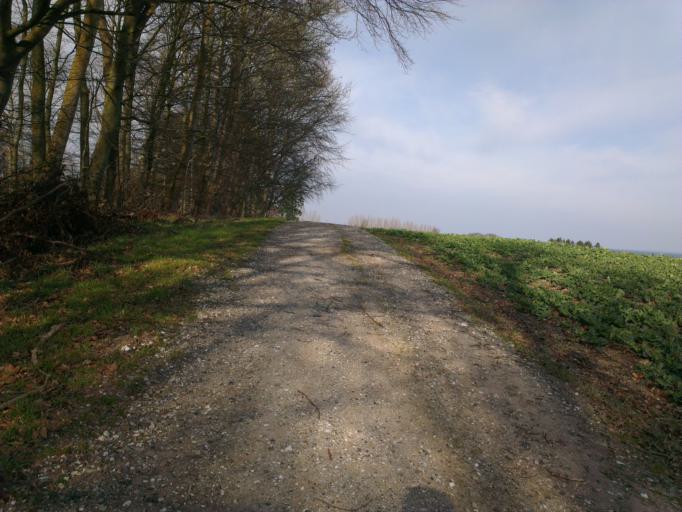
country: DK
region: Capital Region
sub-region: Frederikssund Kommune
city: Jaegerspris
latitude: 55.8111
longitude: 11.9271
